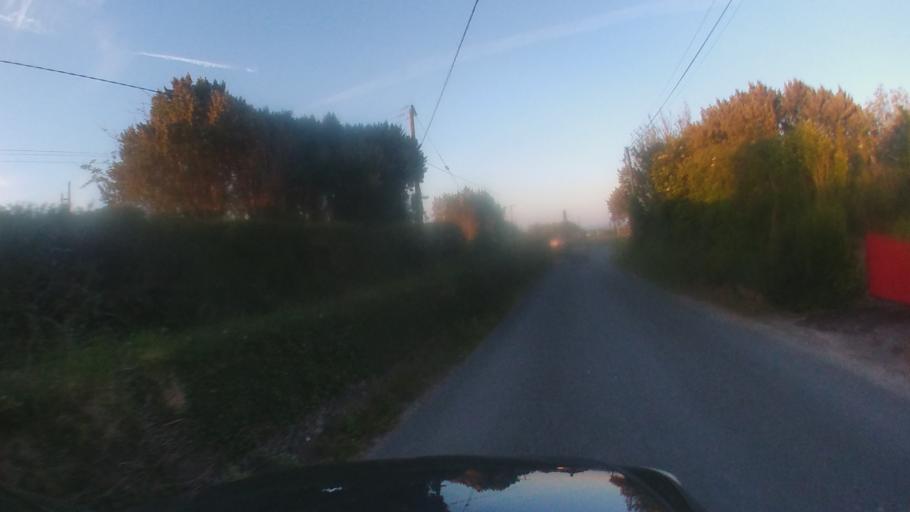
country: IE
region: Leinster
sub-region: Loch Garman
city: Ballygerry
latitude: 52.1977
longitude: -6.3568
